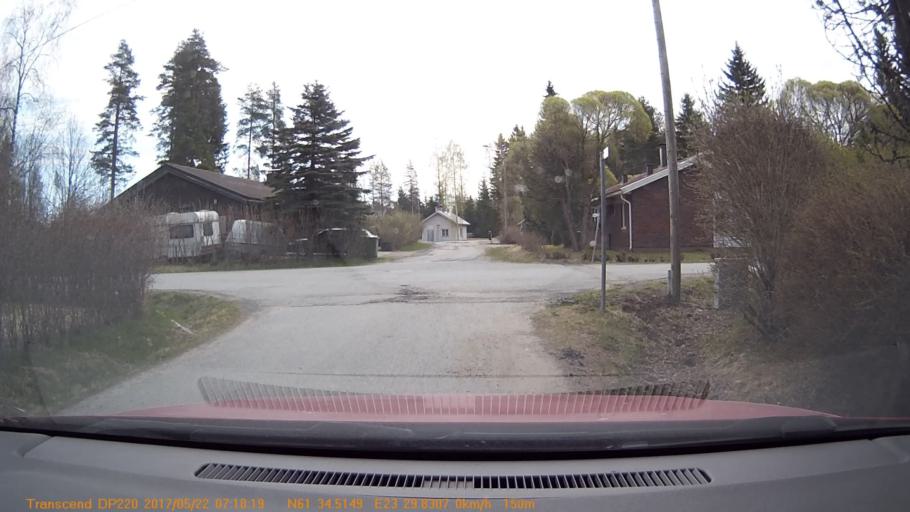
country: FI
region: Pirkanmaa
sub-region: Tampere
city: Yloejaervi
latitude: 61.5753
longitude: 23.4972
